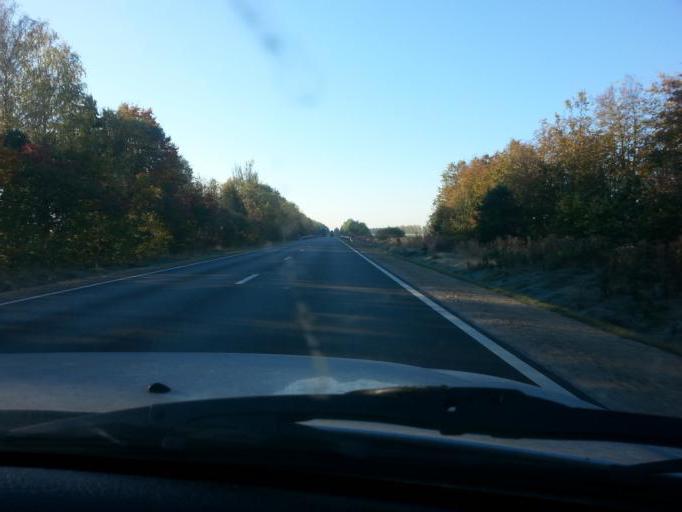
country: LV
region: Jelgava
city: Jelgava
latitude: 56.5191
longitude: 23.7035
